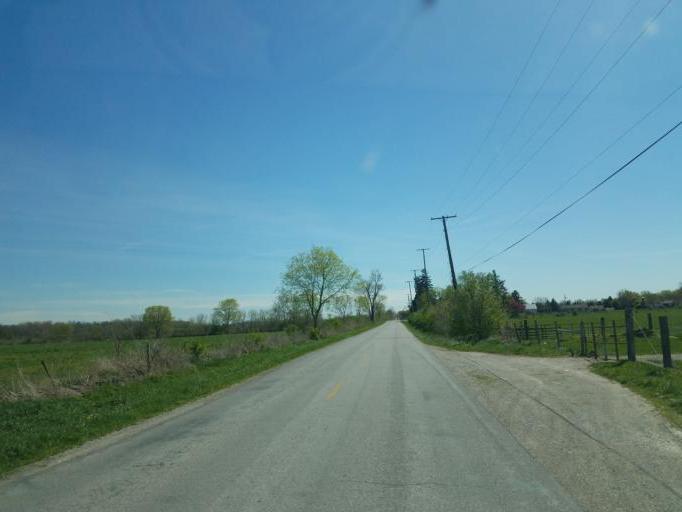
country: US
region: Ohio
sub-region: Erie County
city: Sandusky
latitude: 41.3774
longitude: -82.7871
